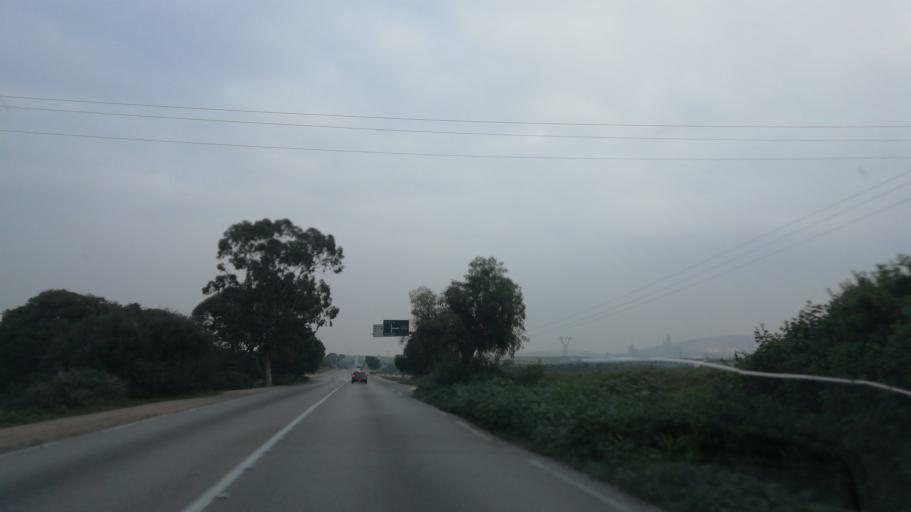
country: DZ
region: Mascara
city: Sig
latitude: 35.5414
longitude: -0.3248
